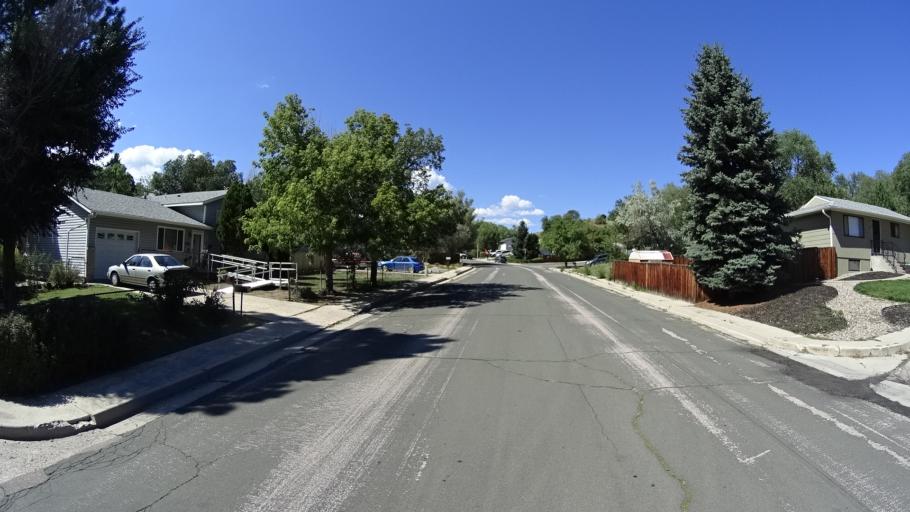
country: US
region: Colorado
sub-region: El Paso County
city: Colorado Springs
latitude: 38.8594
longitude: -104.8576
